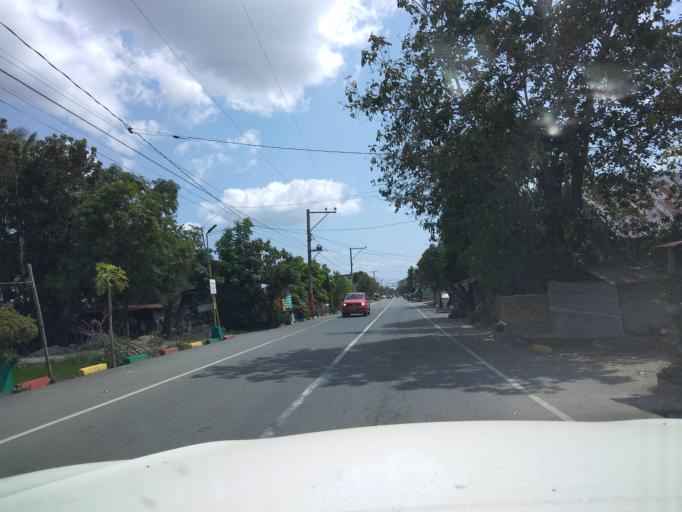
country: PH
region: Central Luzon
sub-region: Province of Pampanga
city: Bahay Pare
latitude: 15.0454
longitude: 120.8785
